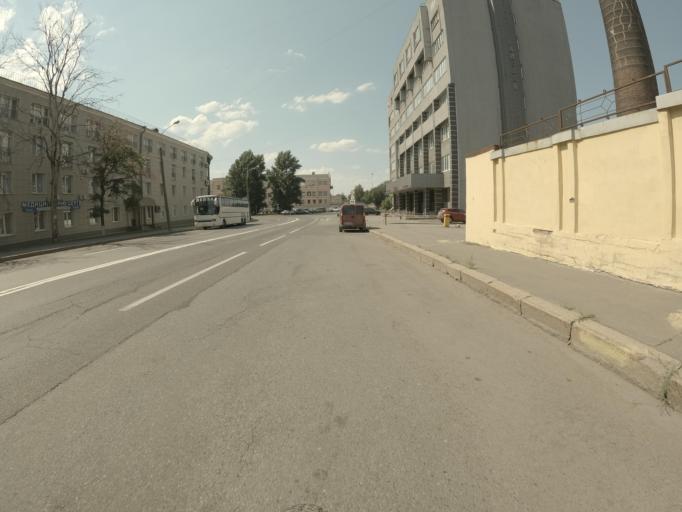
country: RU
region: St.-Petersburg
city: Admiralteisky
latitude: 59.9128
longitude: 30.2605
